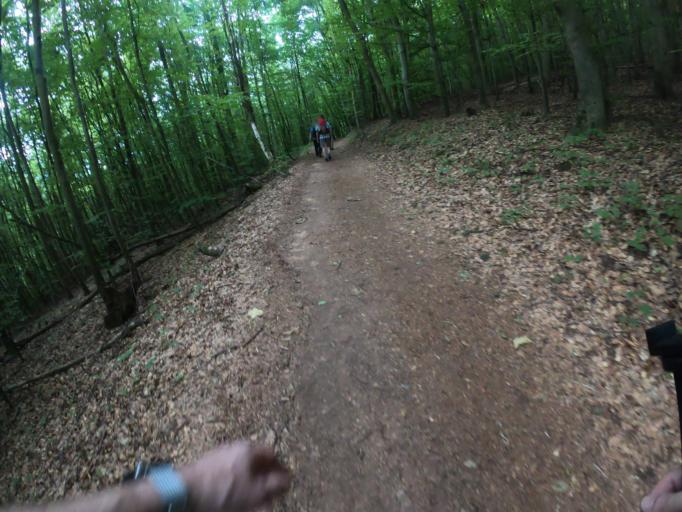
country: DE
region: Rheinland-Pfalz
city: Annweiler am Trifels
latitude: 49.1984
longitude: 7.9823
